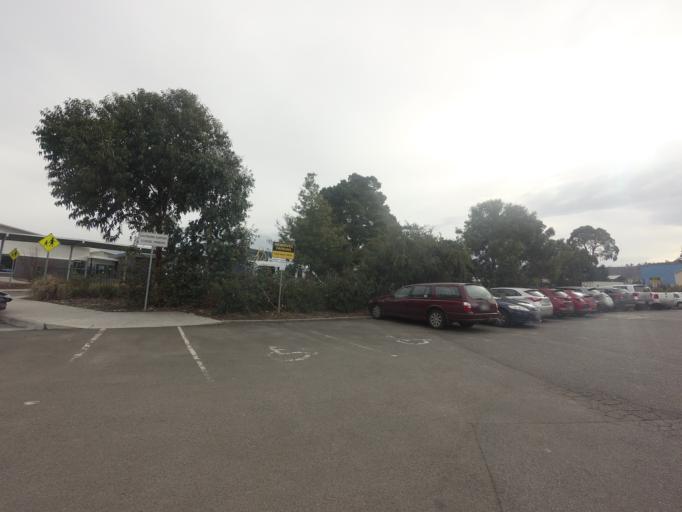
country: AU
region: Tasmania
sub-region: Clarence
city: Howrah
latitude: -42.8797
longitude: 147.4007
